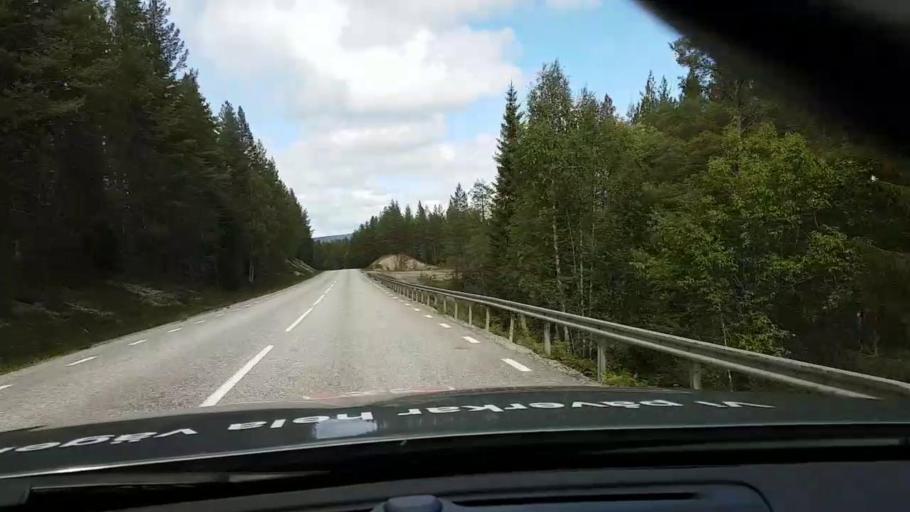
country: SE
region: Vaesternorrland
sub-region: OErnskoeldsviks Kommun
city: Bredbyn
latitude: 63.7004
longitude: 17.7637
